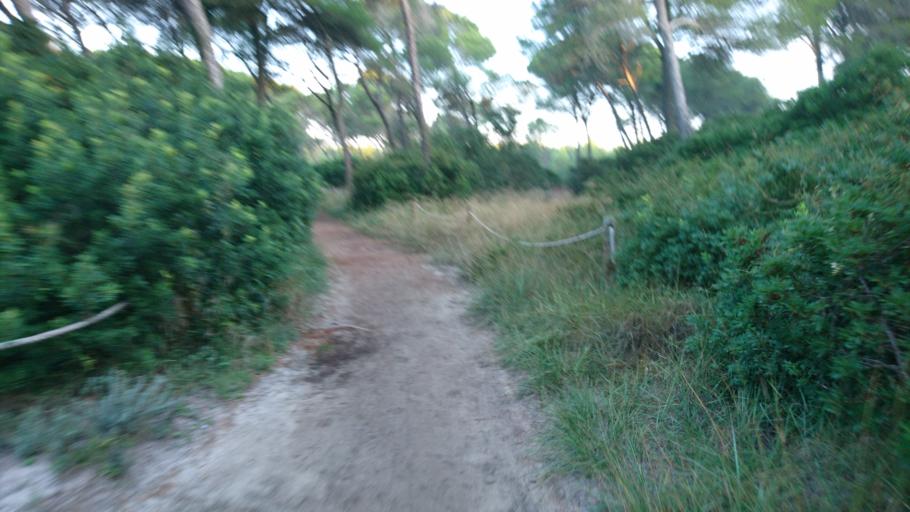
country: ES
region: Balearic Islands
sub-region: Illes Balears
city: Port d'Alcudia
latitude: 39.7828
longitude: 3.1312
